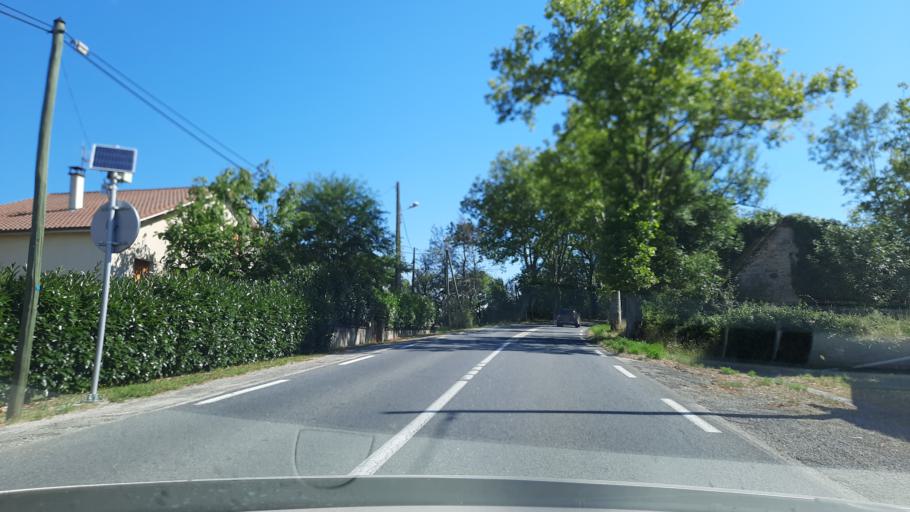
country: FR
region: Midi-Pyrenees
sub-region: Departement de l'Aveyron
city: Villefranche-de-Rouergue
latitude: 44.3223
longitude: 1.8967
